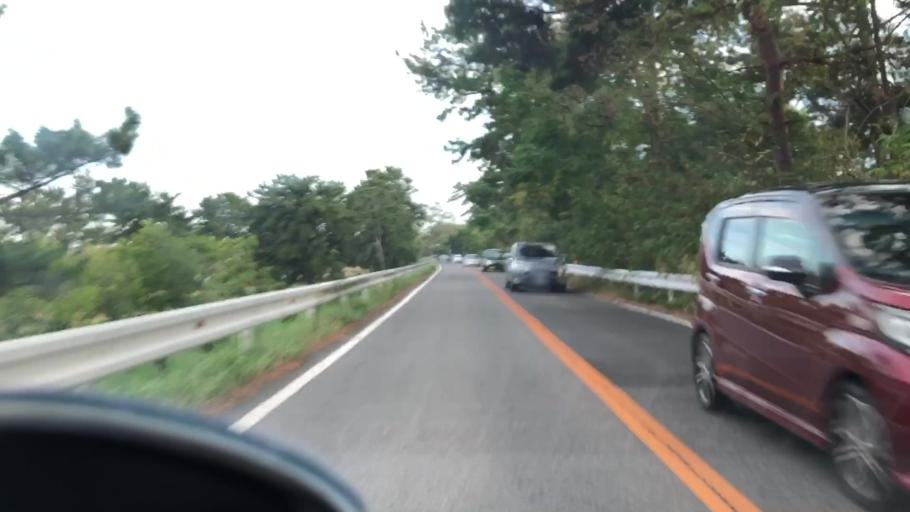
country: JP
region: Hyogo
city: Itami
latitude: 34.7563
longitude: 135.3721
